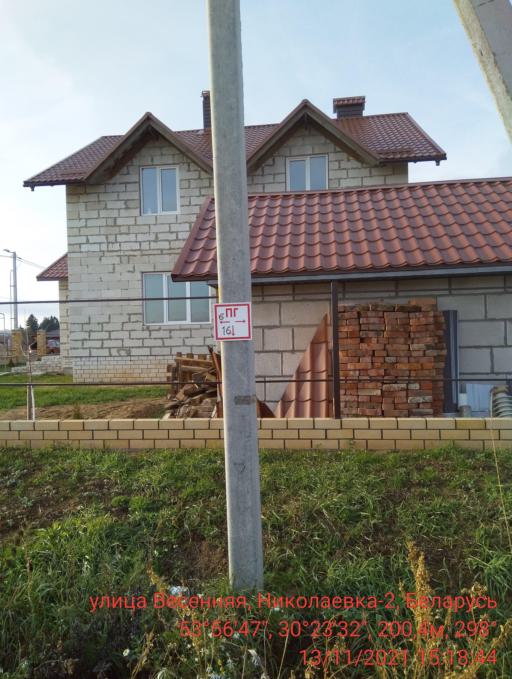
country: BY
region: Mogilev
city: Palykavichy Pyershyya
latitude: 53.9466
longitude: 30.3923
